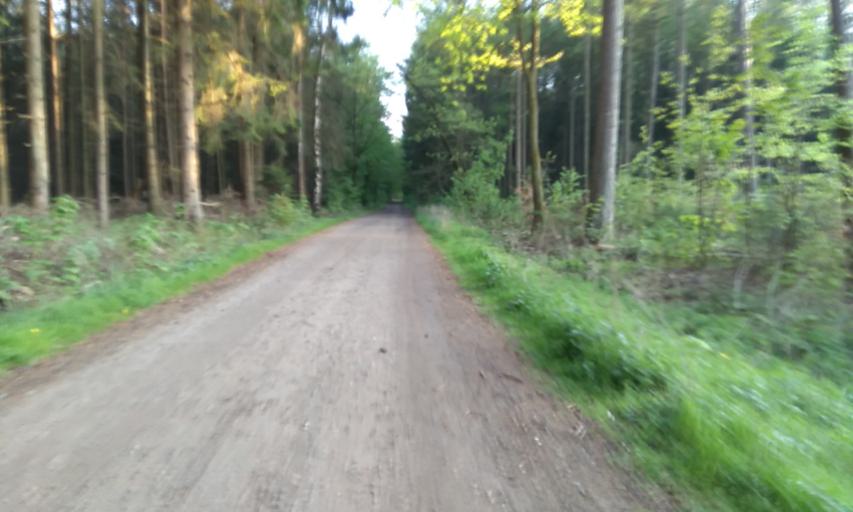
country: DE
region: Lower Saxony
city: Dollern
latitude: 53.5166
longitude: 9.5358
